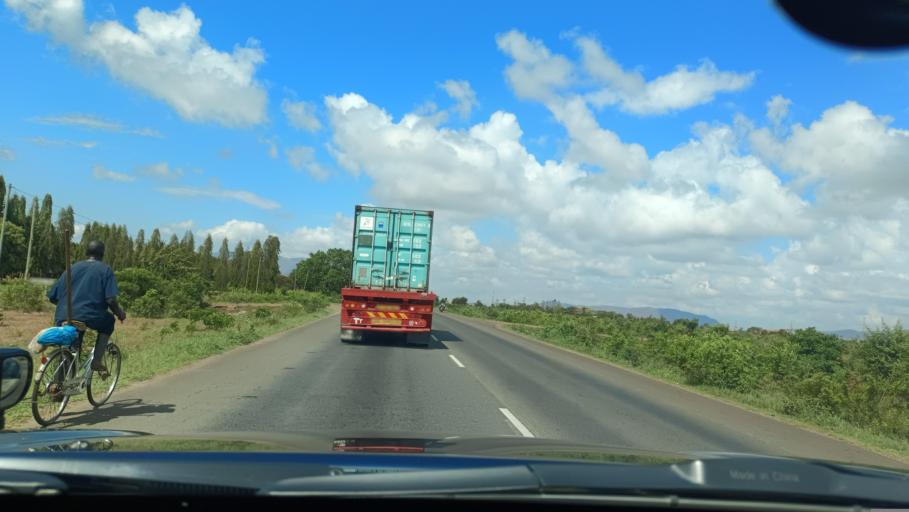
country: TZ
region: Morogoro
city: Morogoro
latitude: -6.8013
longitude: 37.7114
